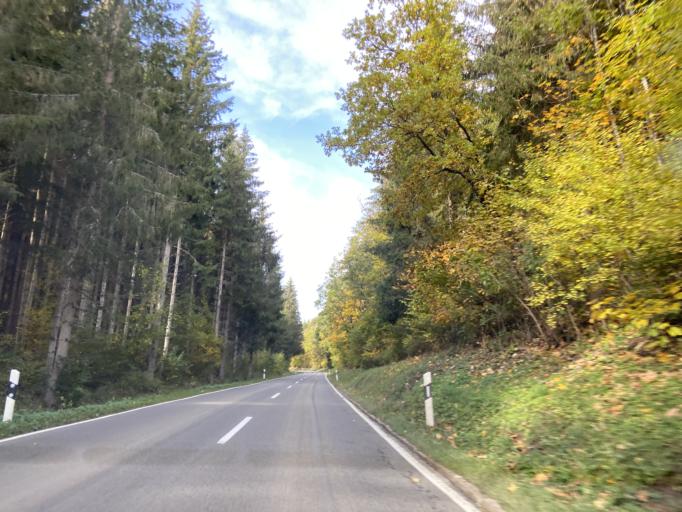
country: DE
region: Baden-Wuerttemberg
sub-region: Tuebingen Region
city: Schwenningen
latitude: 48.0978
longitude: 9.0191
